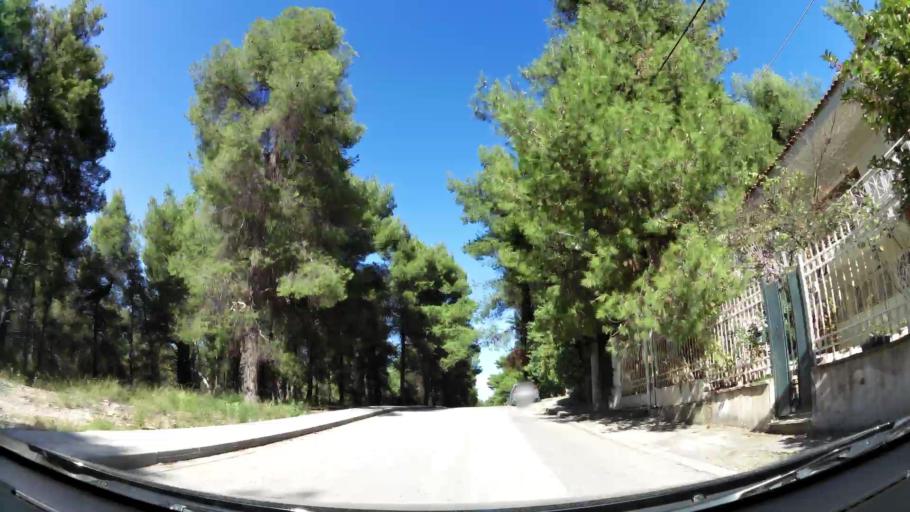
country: GR
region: Attica
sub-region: Nomarchia Anatolikis Attikis
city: Dionysos
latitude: 38.1061
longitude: 23.8719
